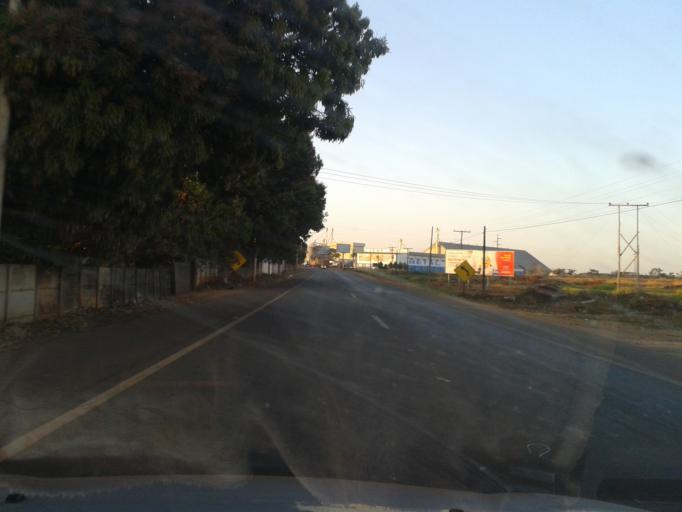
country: BR
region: Goias
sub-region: Itaberai
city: Itaberai
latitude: -16.0507
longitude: -49.7874
